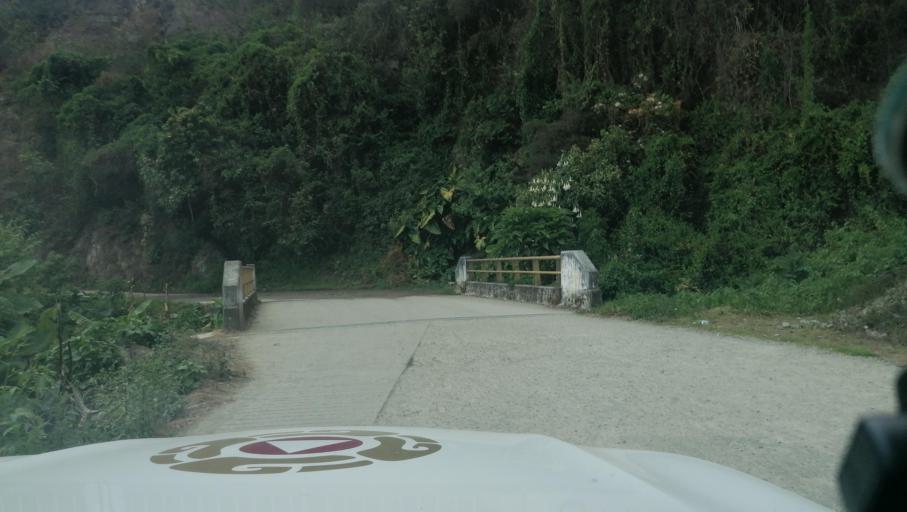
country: GT
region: San Marcos
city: Tacana
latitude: 15.2061
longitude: -92.1839
